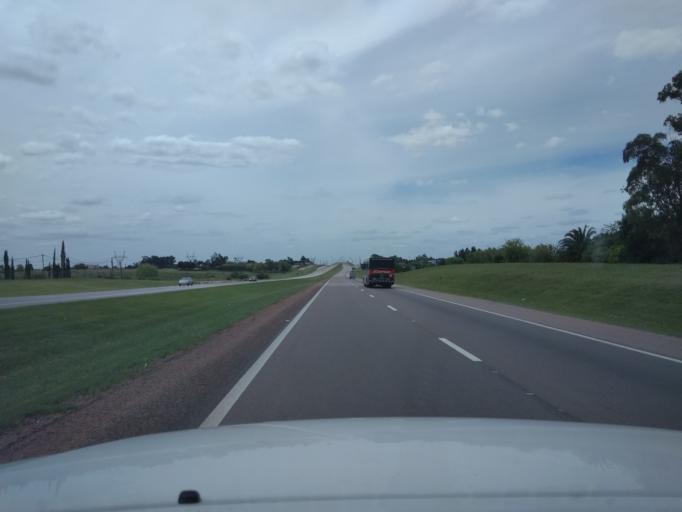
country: UY
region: Canelones
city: Las Piedras
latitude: -34.7312
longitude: -56.2488
